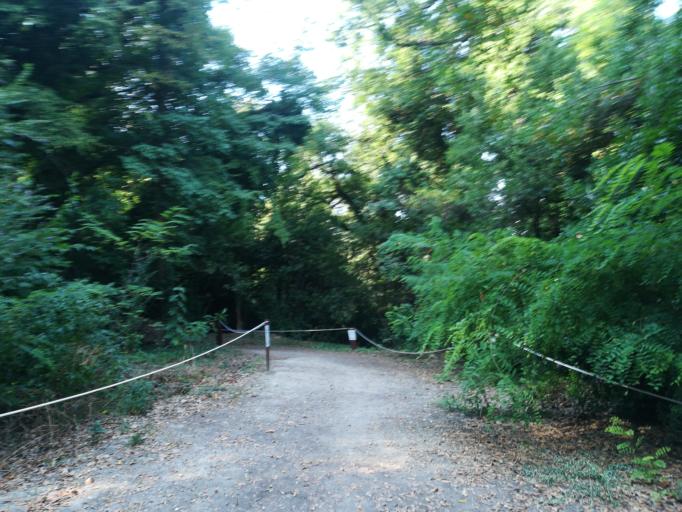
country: IT
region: The Marches
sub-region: Provincia di Macerata
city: Villa Potenza
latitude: 43.2969
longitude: 13.4243
